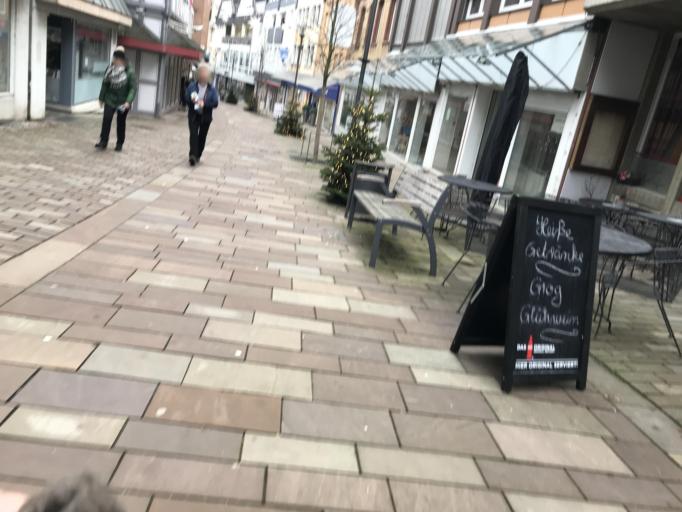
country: DE
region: Hesse
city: Frankenberg
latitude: 51.0601
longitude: 8.7986
